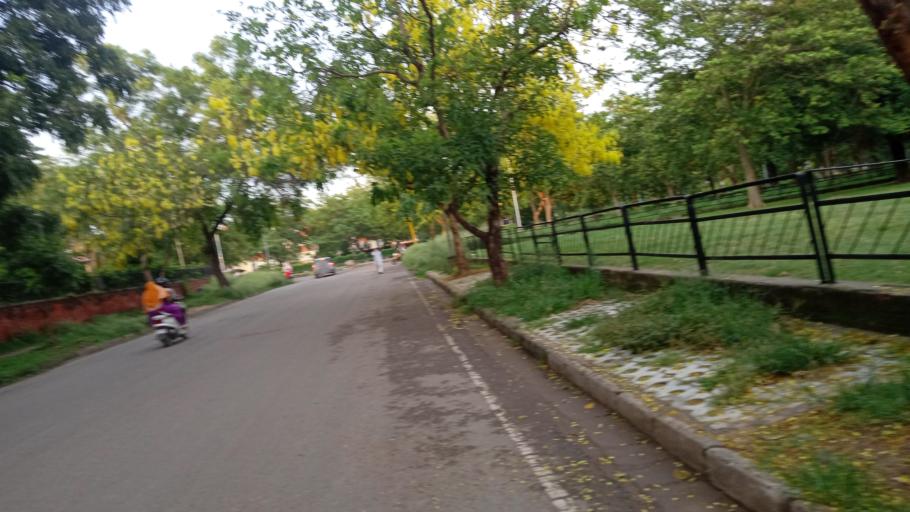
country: IN
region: Chandigarh
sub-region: Chandigarh
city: Chandigarh
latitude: 30.7477
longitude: 76.7507
